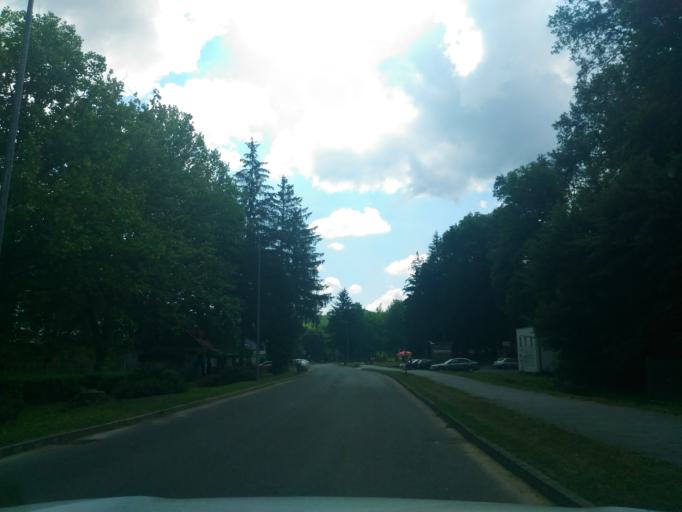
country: HU
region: Baranya
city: Komlo
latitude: 46.1778
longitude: 18.2207
